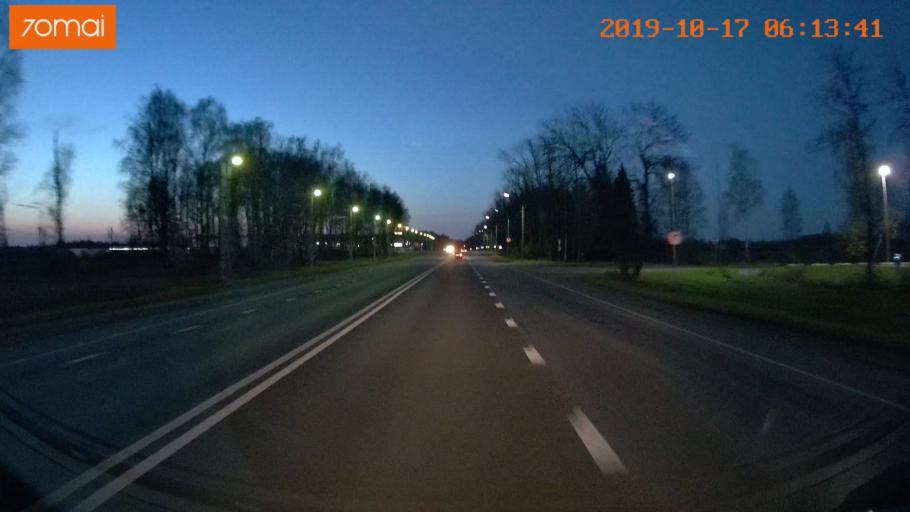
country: RU
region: Ivanovo
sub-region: Gorod Ivanovo
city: Ivanovo
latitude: 56.8954
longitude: 40.9371
